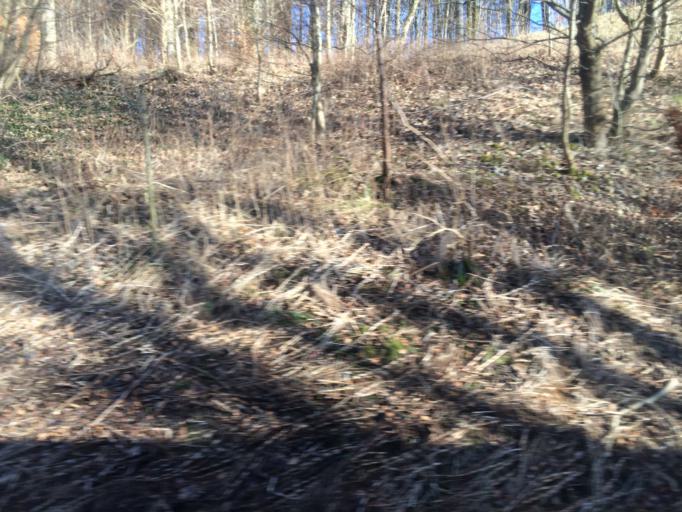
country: DK
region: South Denmark
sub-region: Vejle Kommune
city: Vejle
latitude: 55.7548
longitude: 9.5341
